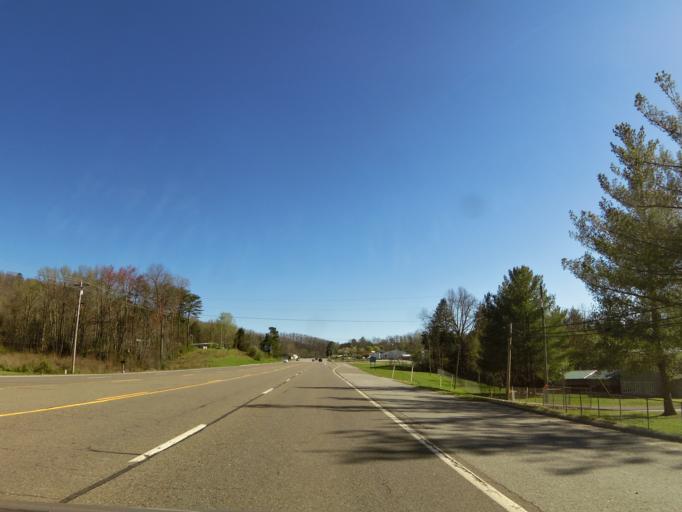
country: US
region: Tennessee
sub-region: Scott County
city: Huntsville
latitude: 36.4315
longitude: -84.5383
